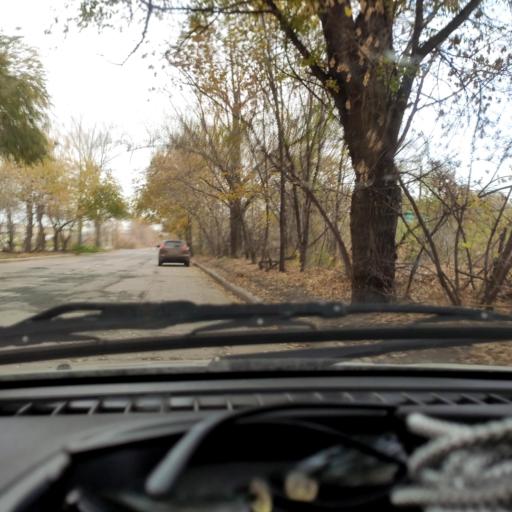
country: RU
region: Samara
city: Tol'yatti
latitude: 53.5236
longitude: 49.4317
